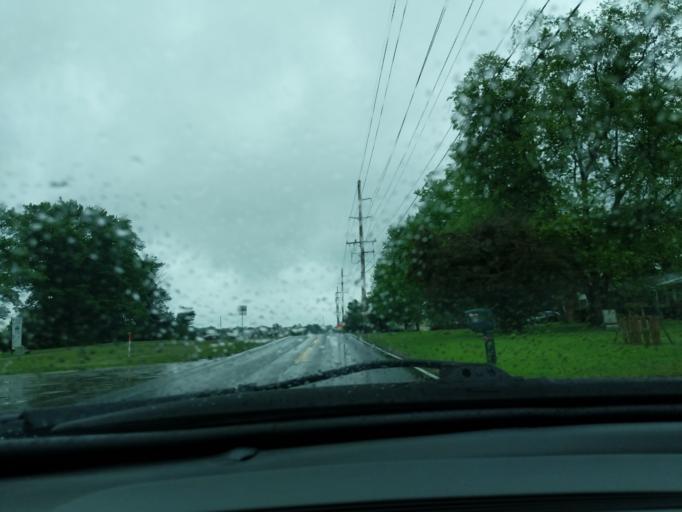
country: US
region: Indiana
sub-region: Hamilton County
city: Noblesville
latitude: 40.0747
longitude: -86.0334
